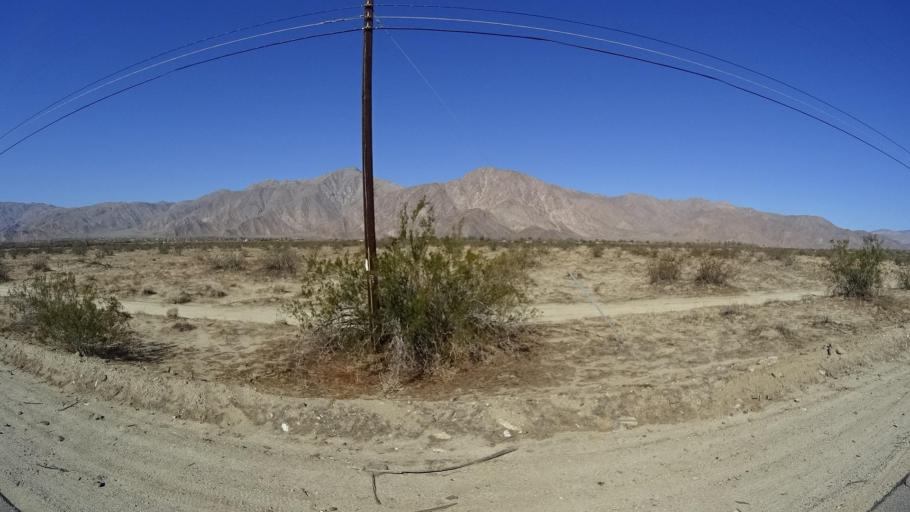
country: US
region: California
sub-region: San Diego County
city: Borrego Springs
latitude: 33.2866
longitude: -116.3663
